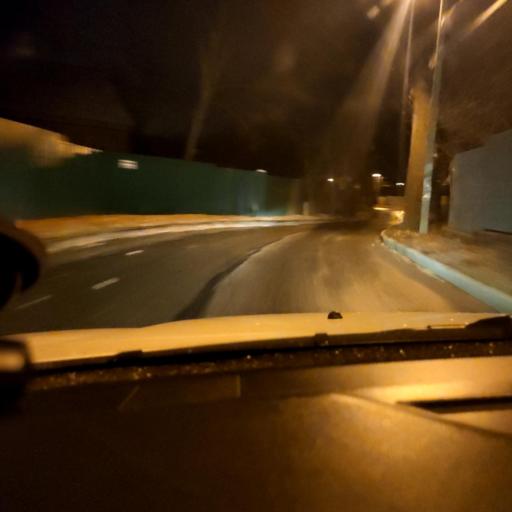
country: RU
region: Samara
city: Samara
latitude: 53.2855
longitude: 50.1982
